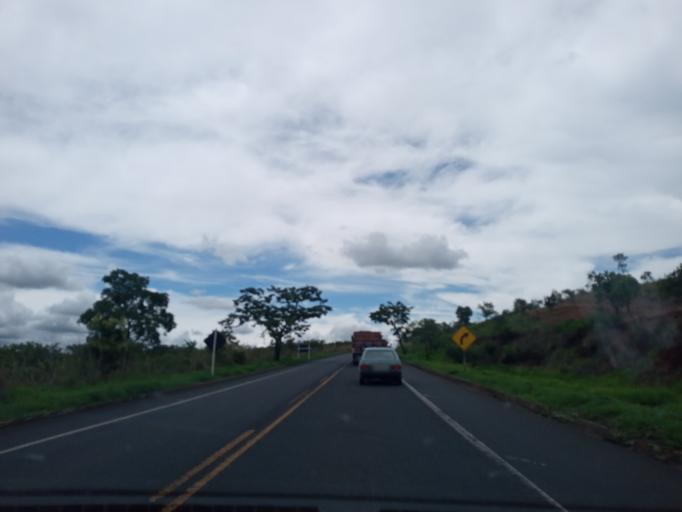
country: BR
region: Minas Gerais
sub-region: Uberlandia
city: Uberlandia
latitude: -19.1688
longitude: -47.8994
